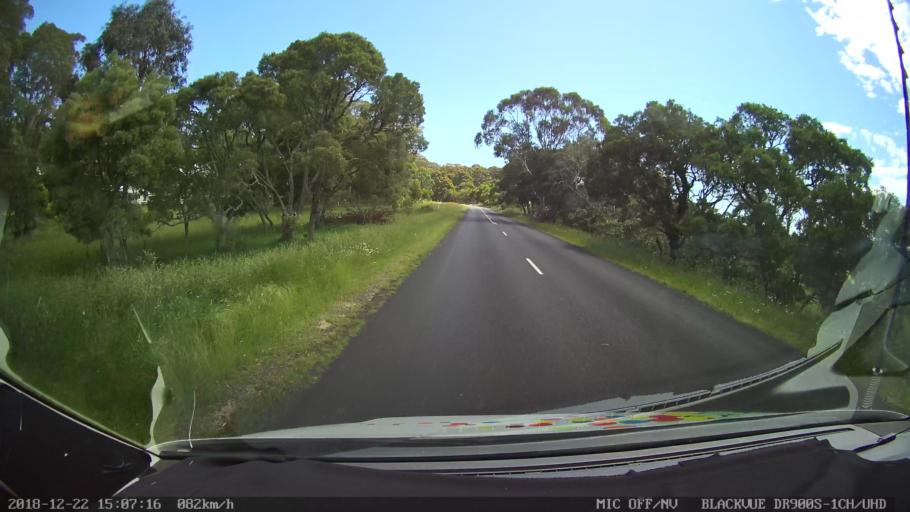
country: AU
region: New South Wales
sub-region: Bellingen
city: Dorrigo
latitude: -30.2988
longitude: 152.4168
